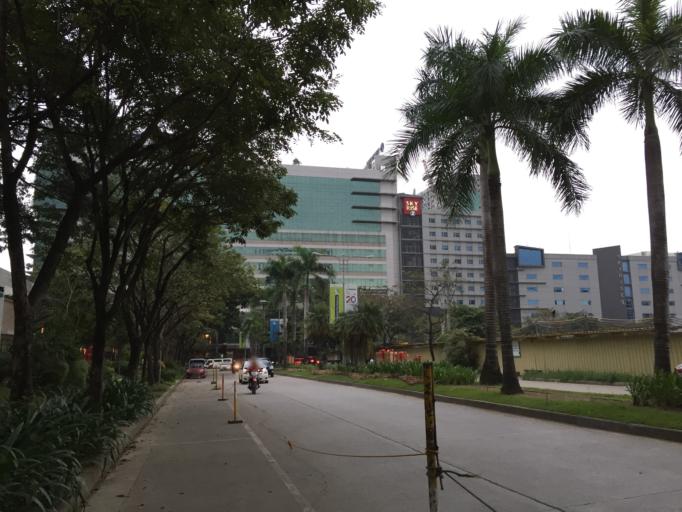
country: PH
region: Central Visayas
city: Mandaue City
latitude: 10.3309
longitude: 123.9063
